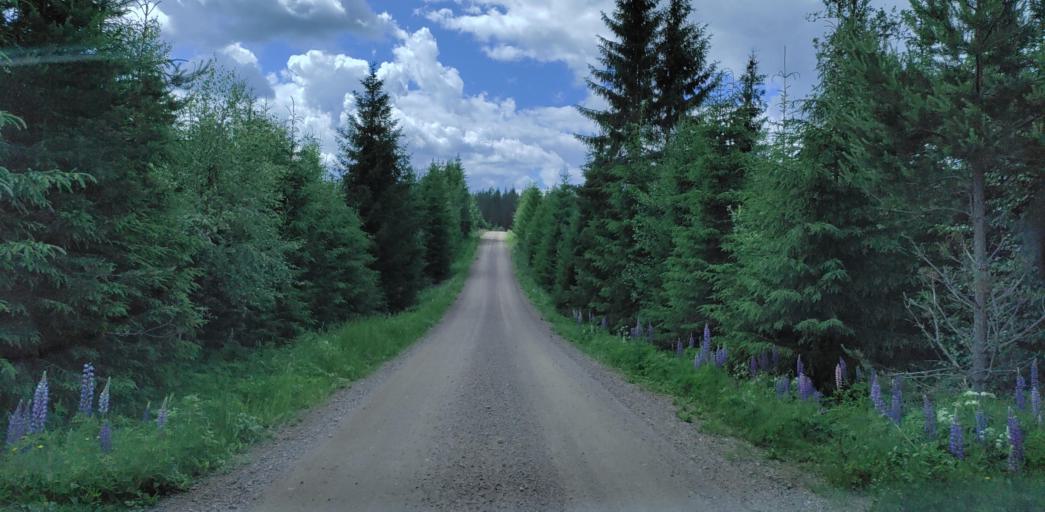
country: SE
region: Vaermland
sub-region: Hagfors Kommun
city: Ekshaerad
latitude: 60.0870
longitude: 13.3264
